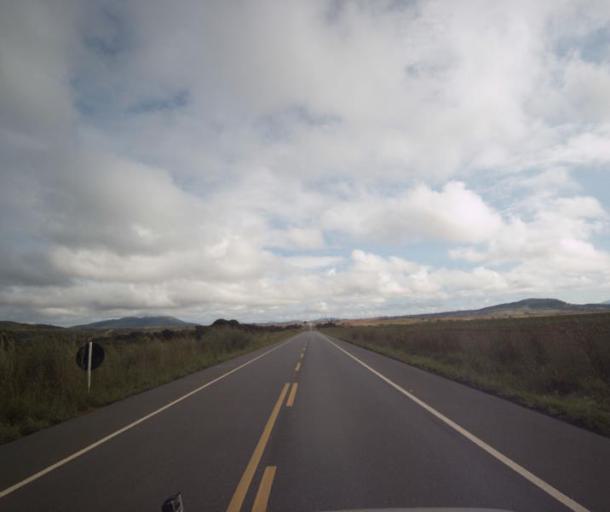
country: BR
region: Goias
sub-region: Barro Alto
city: Barro Alto
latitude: -15.2891
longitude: -48.6784
